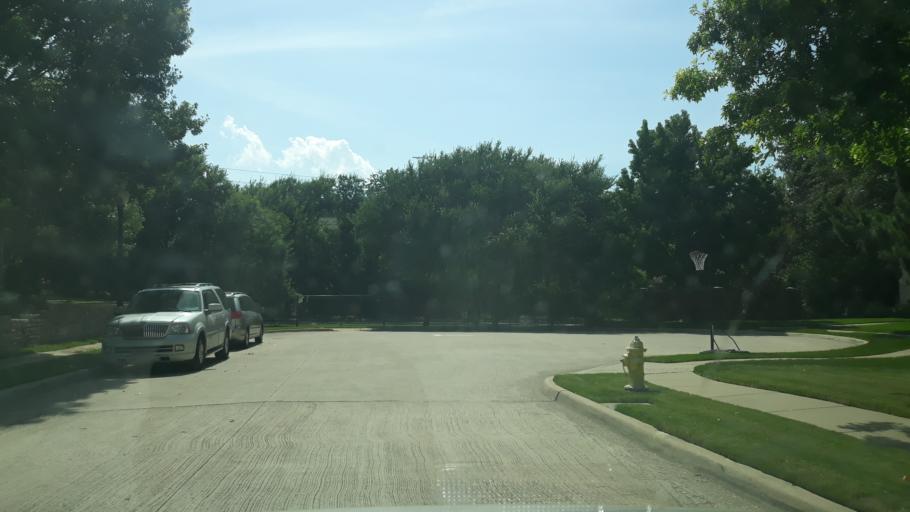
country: US
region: Texas
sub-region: Dallas County
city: Coppell
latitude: 32.9681
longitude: -97.0060
